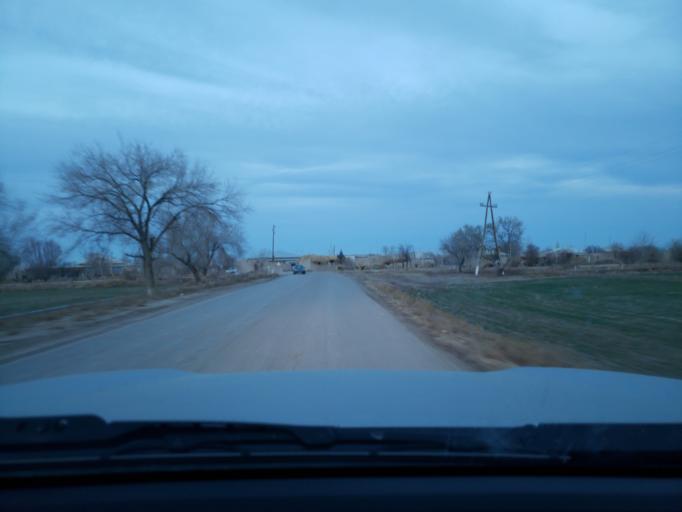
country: TM
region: Dasoguz
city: Tagta
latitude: 41.6291
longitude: 60.0665
